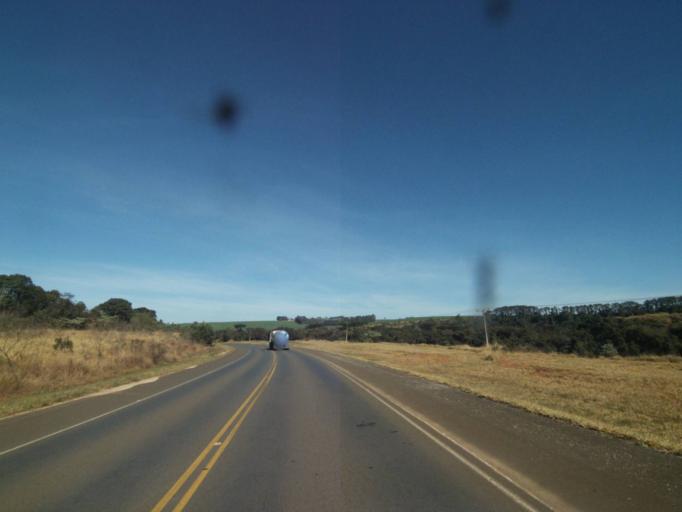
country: BR
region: Parana
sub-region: Tibagi
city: Tibagi
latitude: -24.4755
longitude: -50.4459
